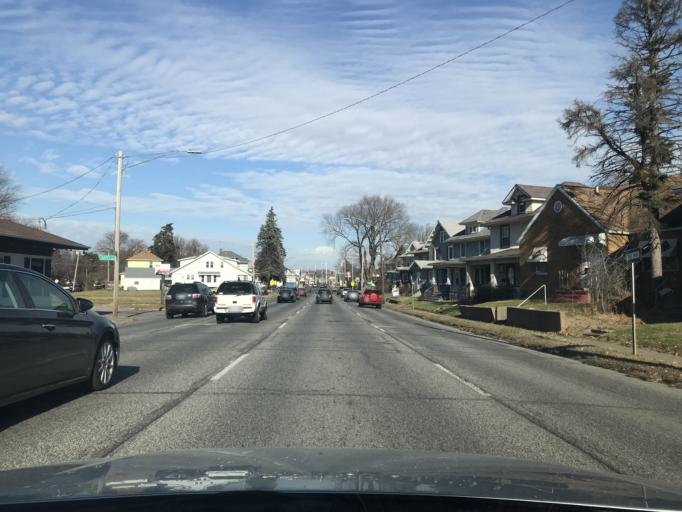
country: US
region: Iowa
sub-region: Scott County
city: Davenport
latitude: 41.5472
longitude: -90.5717
